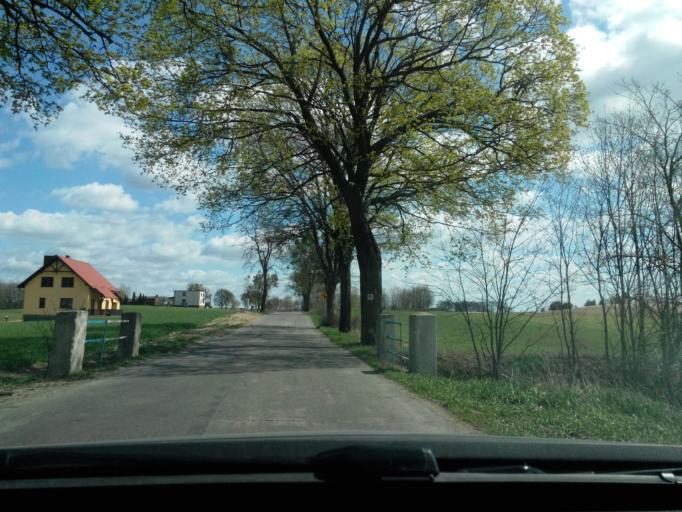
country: PL
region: Warmian-Masurian Voivodeship
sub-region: Powiat nowomiejski
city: Biskupiec
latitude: 53.4471
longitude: 19.3228
